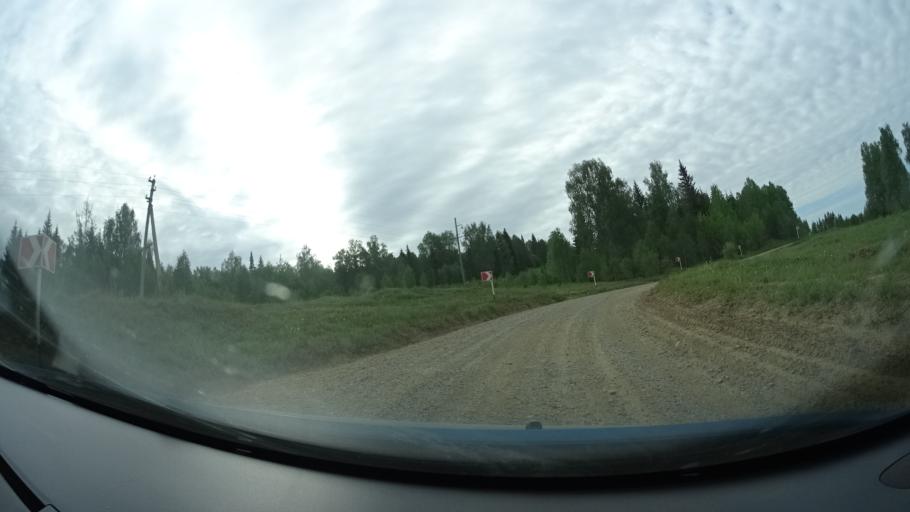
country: RU
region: Perm
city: Kuyeda
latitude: 56.6508
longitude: 55.6982
